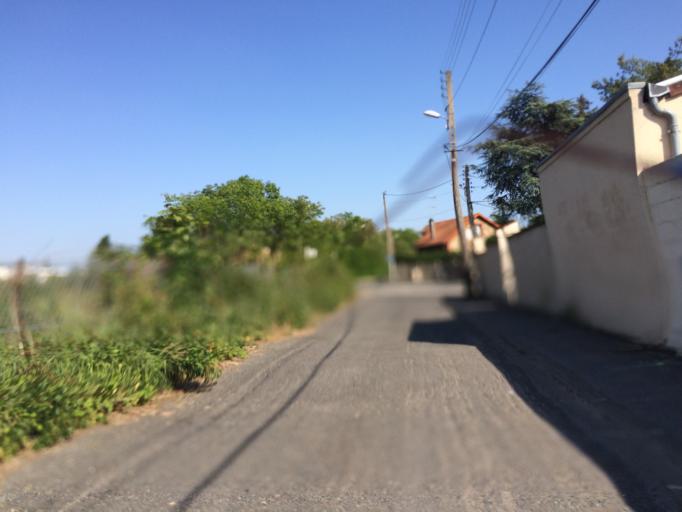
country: FR
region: Ile-de-France
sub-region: Departement de l'Essonne
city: Morsang-sur-Orge
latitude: 48.6665
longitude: 2.3600
